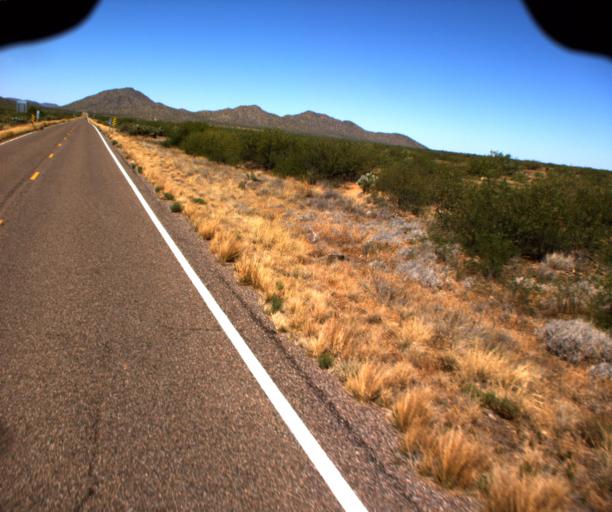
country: US
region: Arizona
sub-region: Yavapai County
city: Congress
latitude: 34.1203
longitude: -112.9584
